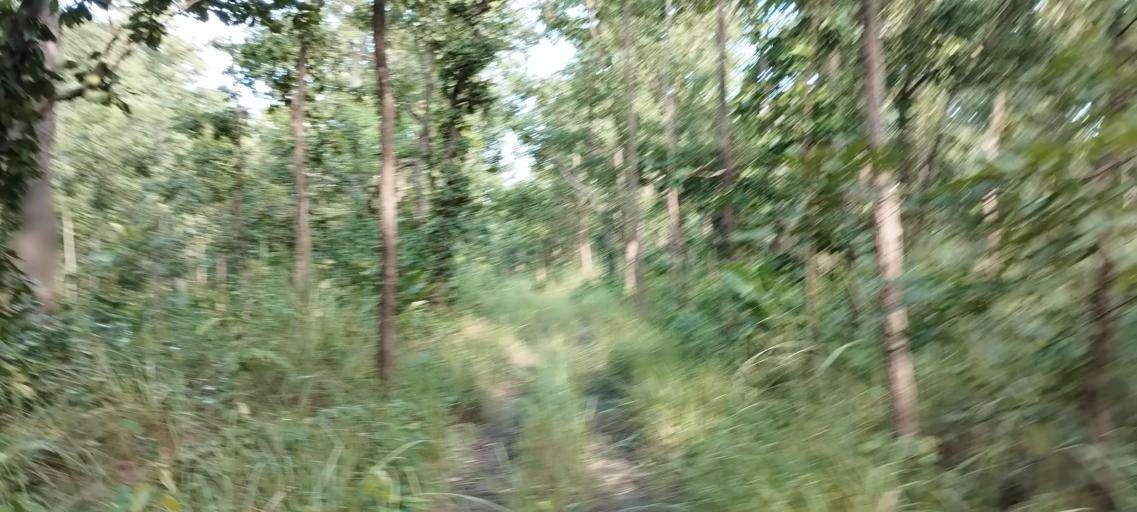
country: NP
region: Far Western
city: Tikapur
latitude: 28.5522
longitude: 81.2804
